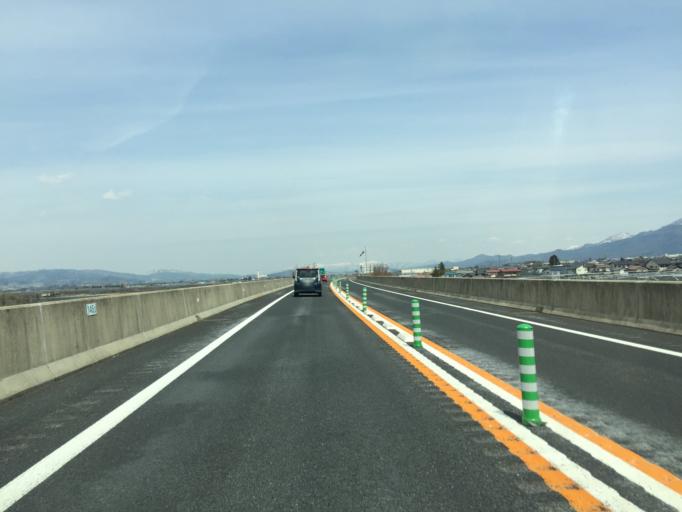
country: JP
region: Yamagata
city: Tendo
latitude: 38.3959
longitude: 140.3427
